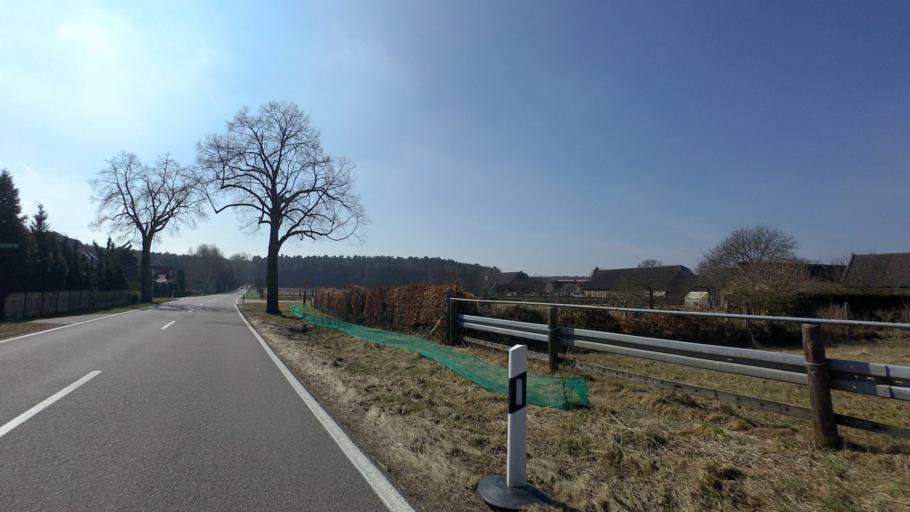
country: DE
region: Saxony-Anhalt
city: Nudersdorf
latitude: 51.9925
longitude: 12.5842
